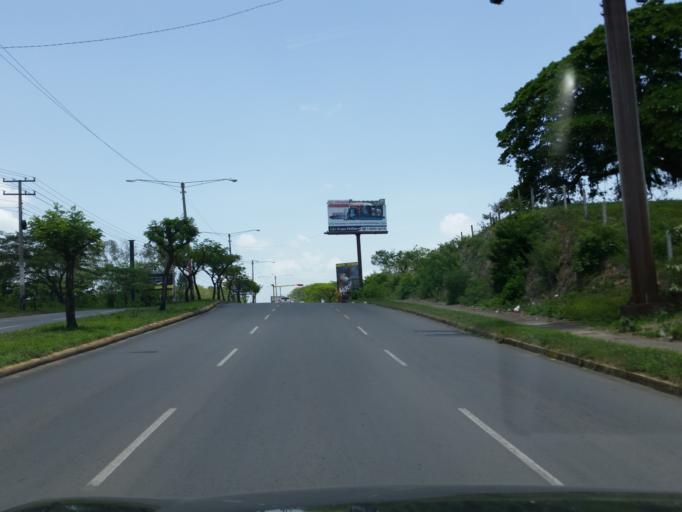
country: NI
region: Managua
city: Managua
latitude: 12.1091
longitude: -86.2805
